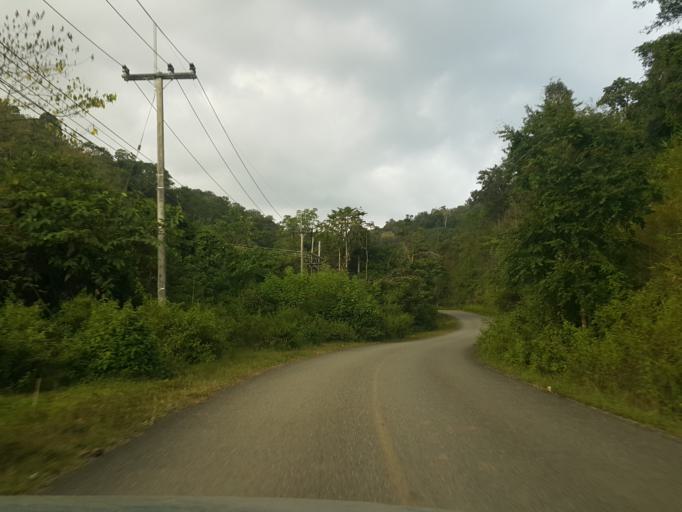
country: TH
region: Mae Hong Son
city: Khun Yuam
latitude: 18.7624
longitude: 98.1859
